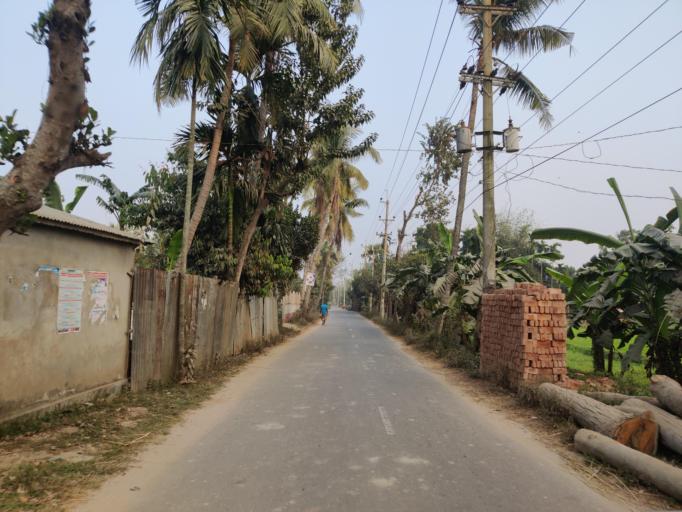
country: BD
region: Dhaka
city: Bajitpur
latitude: 24.1586
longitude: 90.7552
